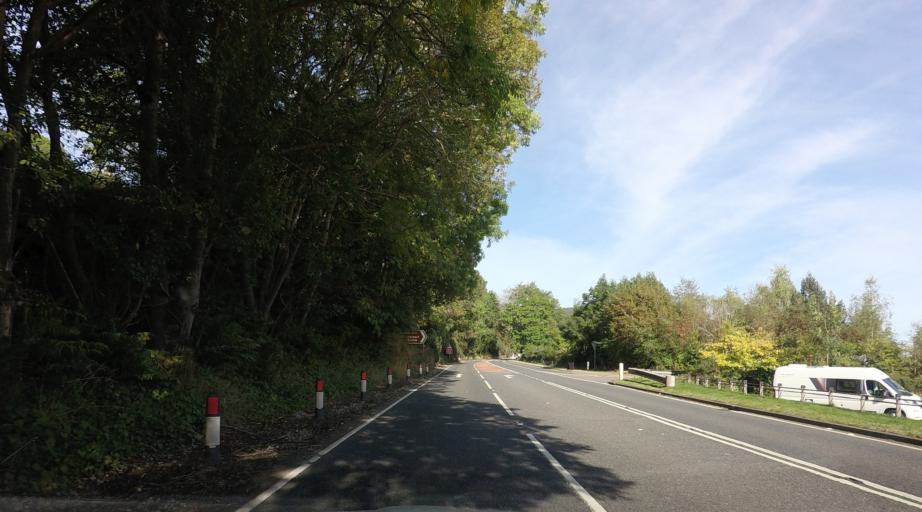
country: GB
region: Scotland
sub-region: Highland
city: Beauly
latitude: 57.3246
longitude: -4.4455
